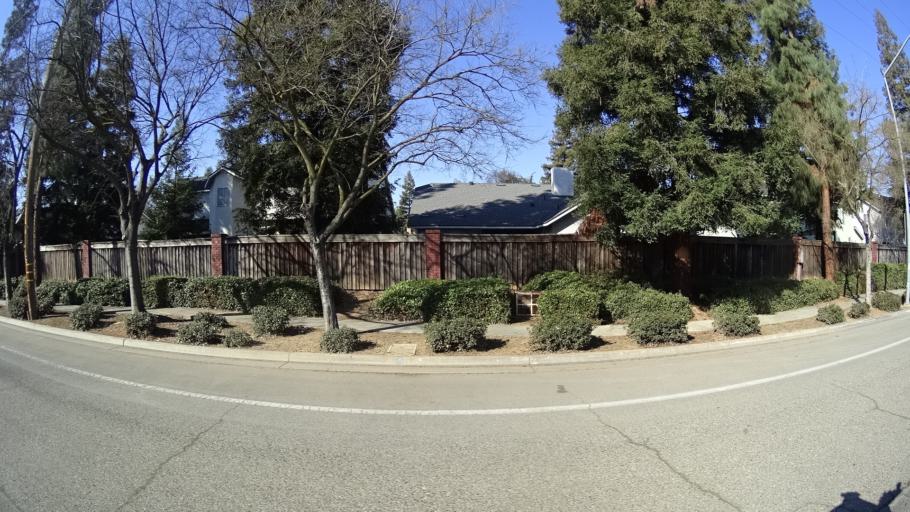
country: US
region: California
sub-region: Fresno County
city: Clovis
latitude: 36.8478
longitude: -119.7478
